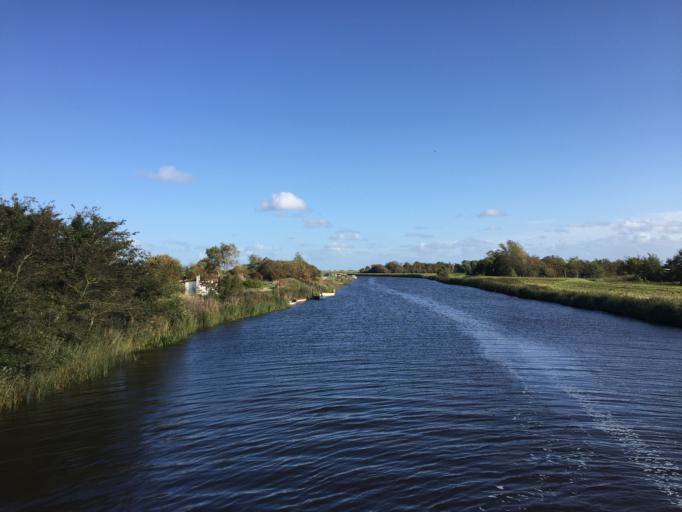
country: DE
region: Schleswig-Holstein
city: Klanxbull
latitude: 54.9566
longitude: 8.6827
